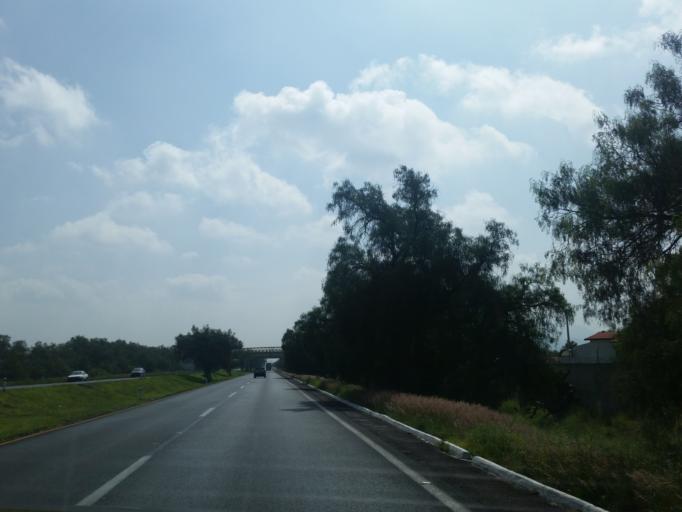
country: MX
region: Mexico
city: Acolman
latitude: 19.6238
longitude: -98.9364
